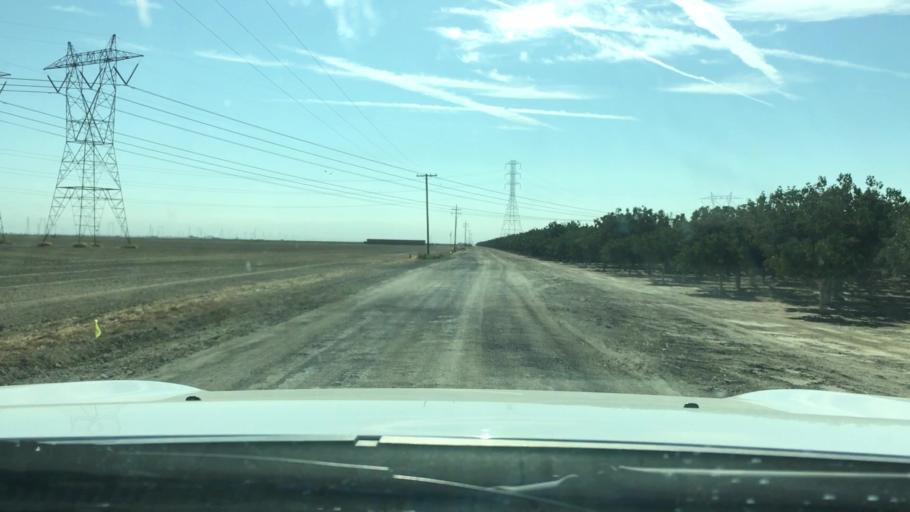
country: US
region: California
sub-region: Kern County
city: Buttonwillow
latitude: 35.3767
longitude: -119.4023
